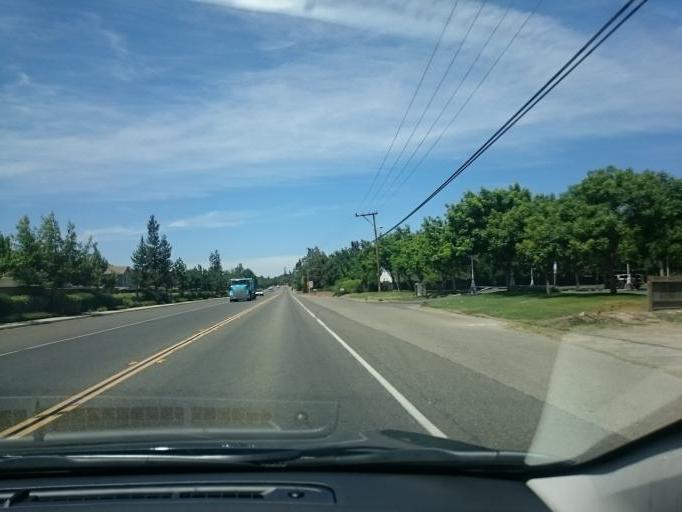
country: US
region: California
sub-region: Stanislaus County
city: Waterford
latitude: 37.6397
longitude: -120.7438
